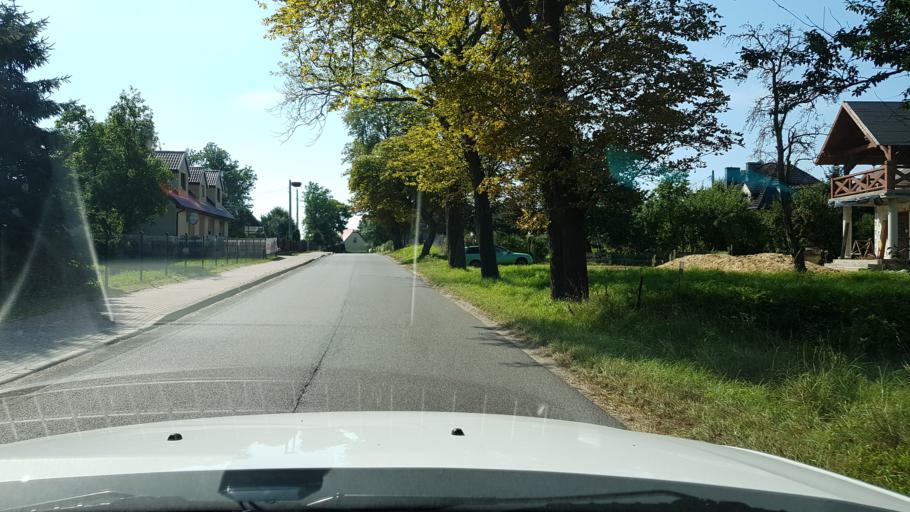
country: PL
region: West Pomeranian Voivodeship
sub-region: Powiat koszalinski
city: Sianow
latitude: 54.2690
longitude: 16.2383
